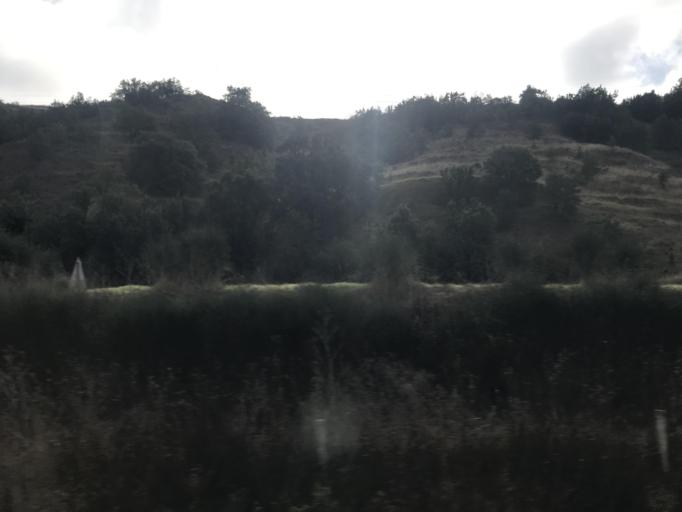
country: ES
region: Castille and Leon
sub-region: Provincia de Burgos
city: Pradanos de Bureba
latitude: 42.5005
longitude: -3.3467
